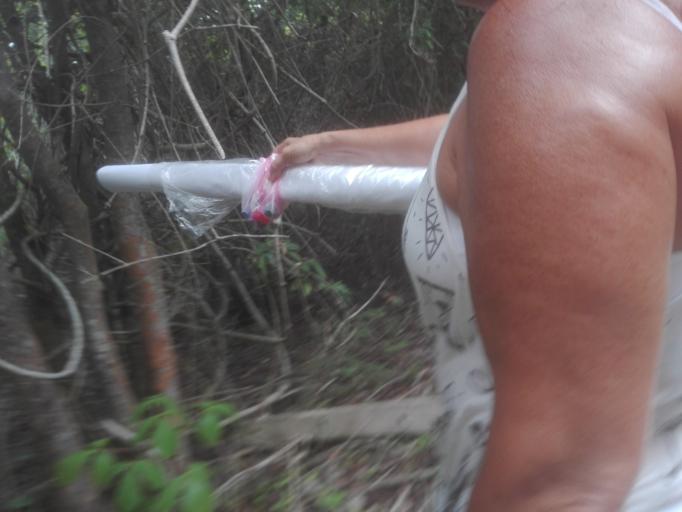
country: CO
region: Bolivar
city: Turbana
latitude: 10.1734
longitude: -75.7454
